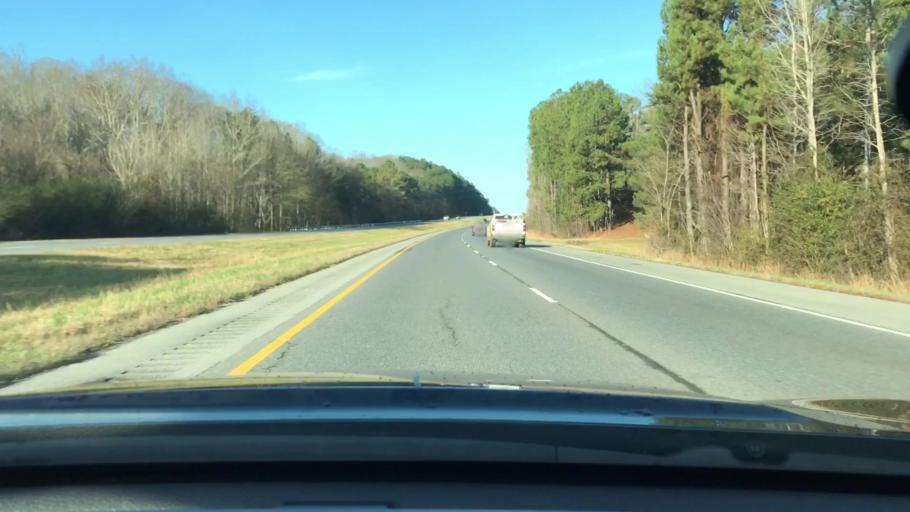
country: US
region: Alabama
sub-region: Shelby County
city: Harpersville
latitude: 33.3522
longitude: -86.4767
